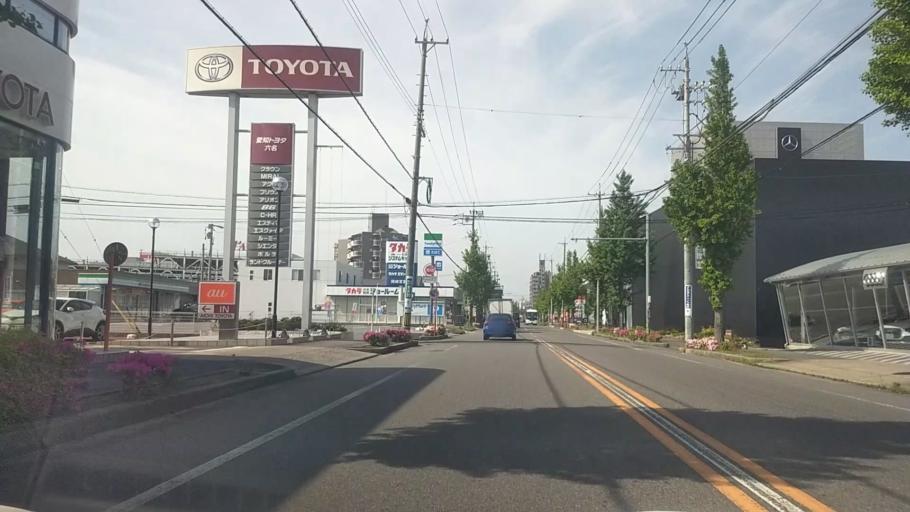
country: JP
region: Aichi
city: Okazaki
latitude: 34.9366
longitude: 137.1475
